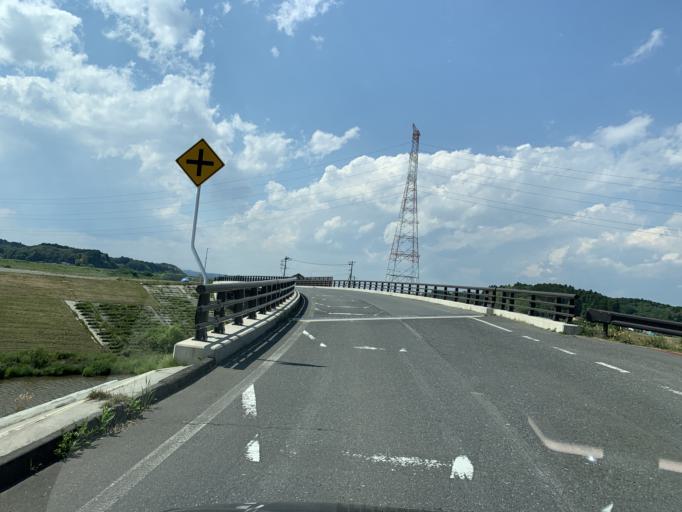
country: JP
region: Miyagi
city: Matsushima
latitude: 38.4288
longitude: 141.1257
